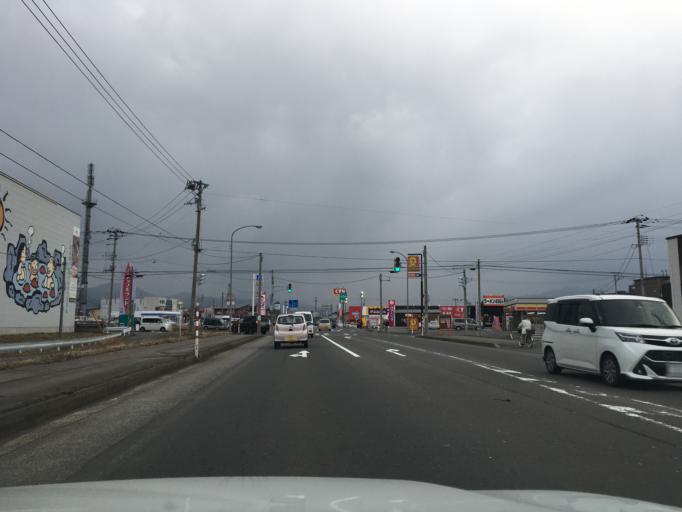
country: JP
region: Aomori
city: Kuroishi
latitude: 40.5868
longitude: 140.5689
